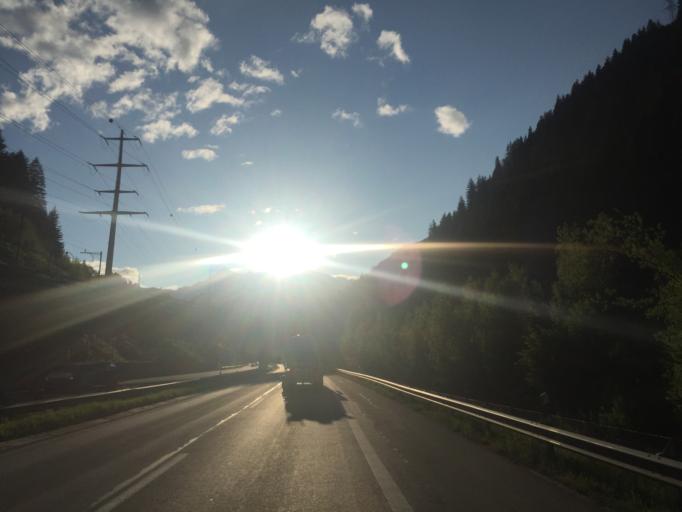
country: CH
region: Ticino
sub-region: Leventina District
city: Airolo
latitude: 46.5175
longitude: 8.6562
